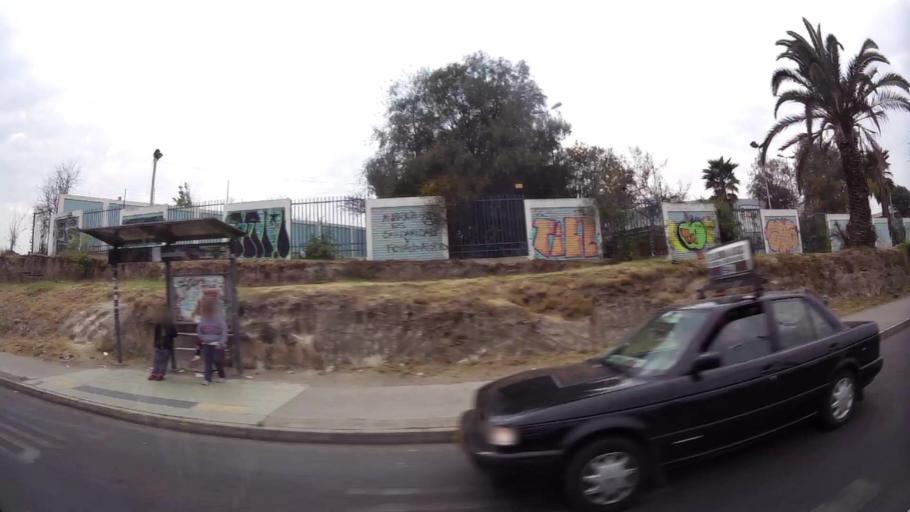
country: CL
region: Santiago Metropolitan
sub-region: Provincia de Santiago
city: Lo Prado
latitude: -33.4876
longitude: -70.7240
